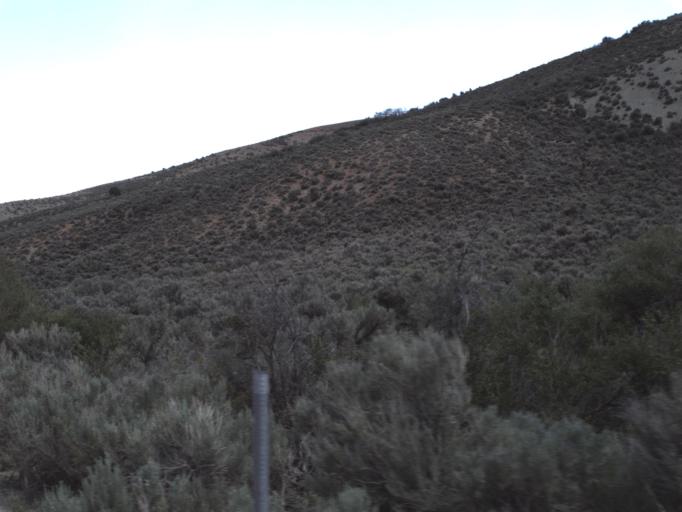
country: US
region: Utah
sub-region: Rich County
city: Randolph
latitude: 41.5008
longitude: -111.3160
